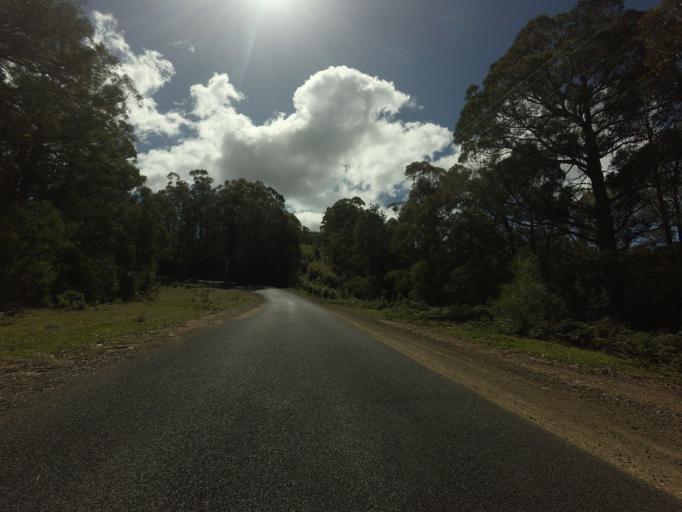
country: AU
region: Tasmania
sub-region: Break O'Day
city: St Helens
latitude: -41.6408
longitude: 148.2428
